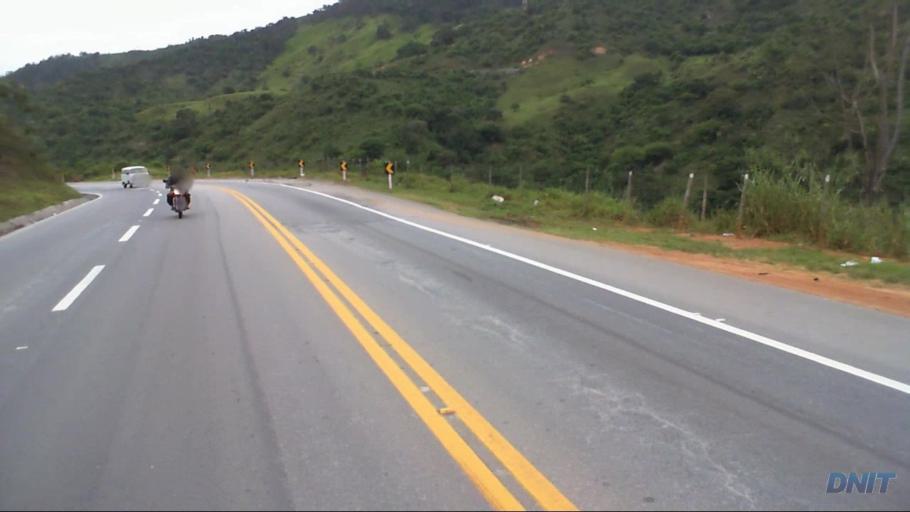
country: BR
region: Minas Gerais
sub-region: Timoteo
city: Timoteo
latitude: -19.6380
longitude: -42.8081
